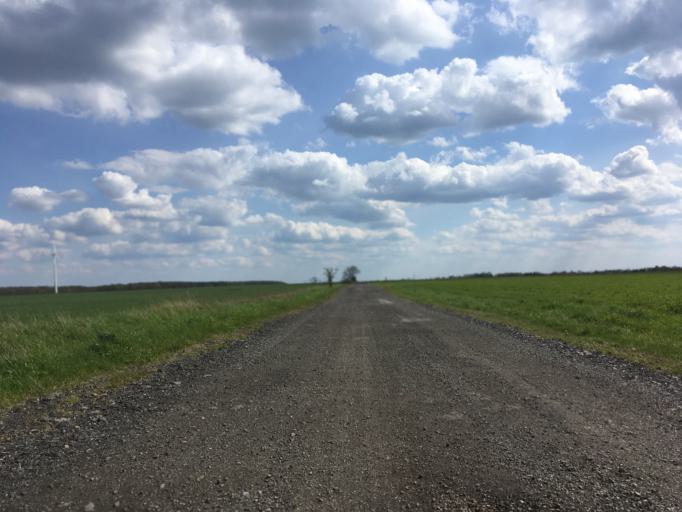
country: DE
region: Brandenburg
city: Werneuchen
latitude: 52.6097
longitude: 13.6996
